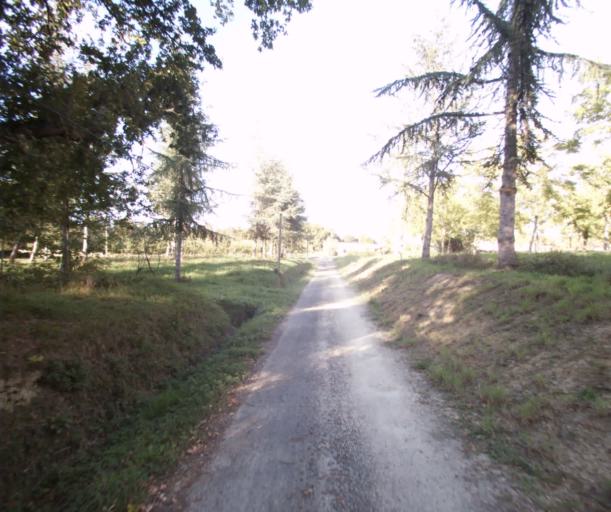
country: FR
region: Midi-Pyrenees
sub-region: Departement du Gers
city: Eauze
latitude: 43.8623
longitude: 0.0244
